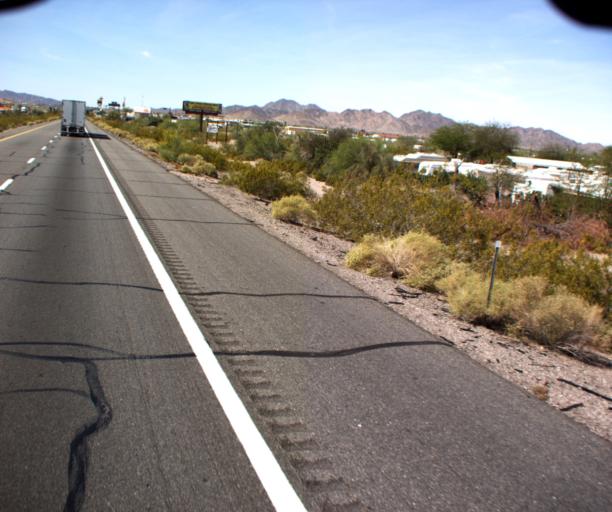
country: US
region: Arizona
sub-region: La Paz County
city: Quartzsite
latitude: 33.6621
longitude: -114.2255
